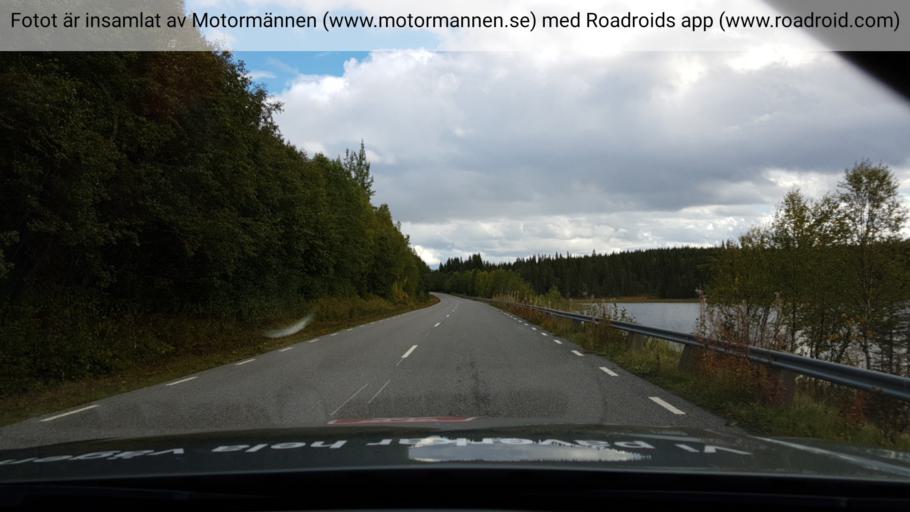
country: SE
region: Jaemtland
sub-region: Are Kommun
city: Are
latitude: 63.6814
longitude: 13.0269
